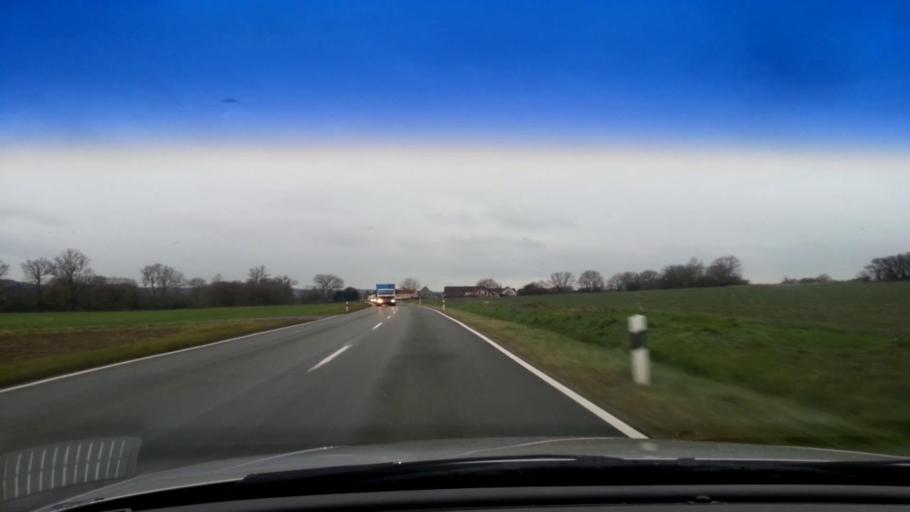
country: DE
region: Bavaria
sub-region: Upper Franconia
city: Pettstadt
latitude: 49.8266
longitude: 10.9030
